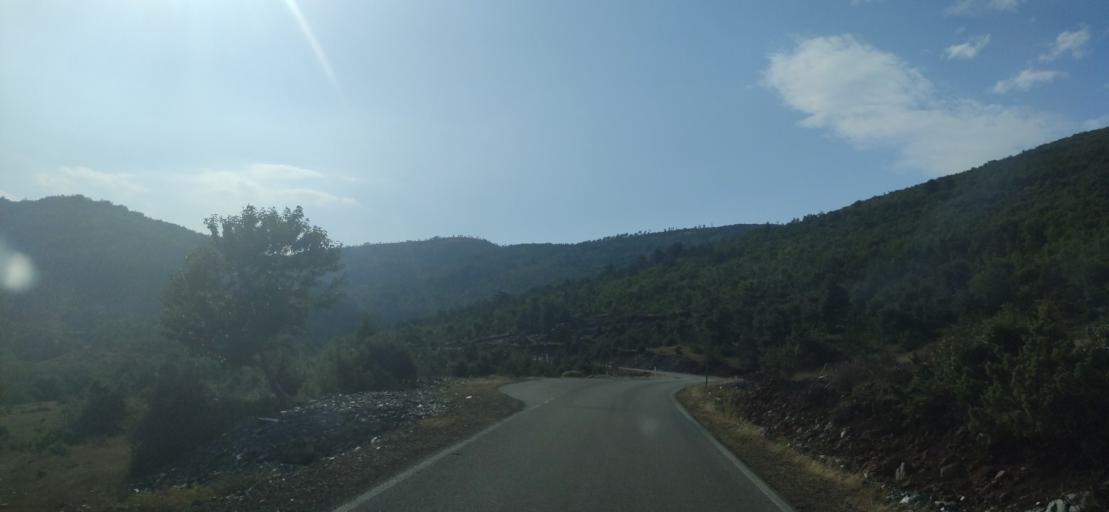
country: AL
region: Shkoder
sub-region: Rrethi i Pukes
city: Iballe
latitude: 42.1780
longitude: 20.0024
